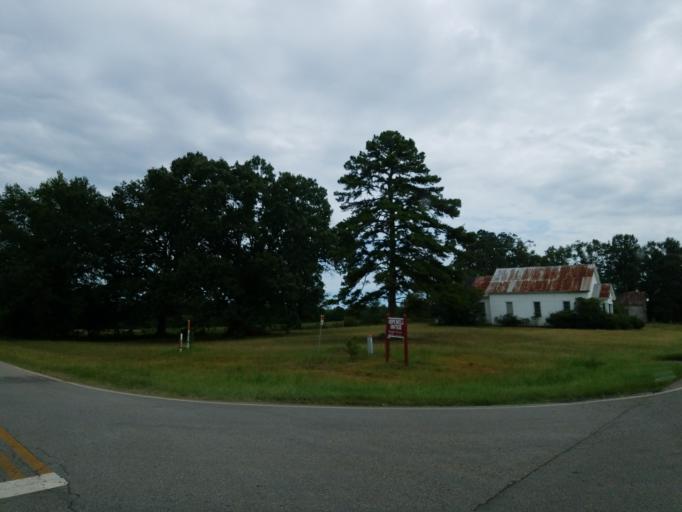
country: US
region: Georgia
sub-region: Monroe County
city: Forsyth
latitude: 32.9816
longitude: -84.0105
